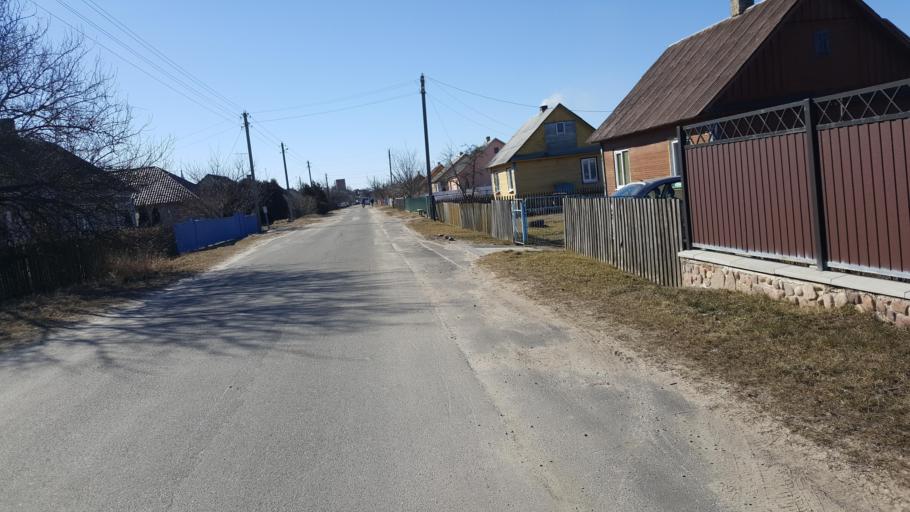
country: BY
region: Brest
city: Kamyanyets
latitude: 52.4084
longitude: 23.8326
